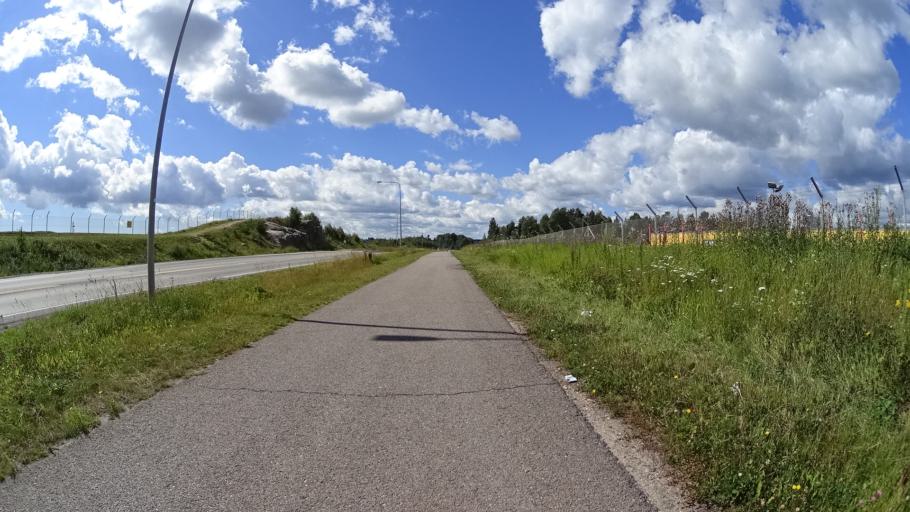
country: FI
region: Uusimaa
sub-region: Helsinki
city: Vantaa
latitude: 60.3176
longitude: 24.9070
